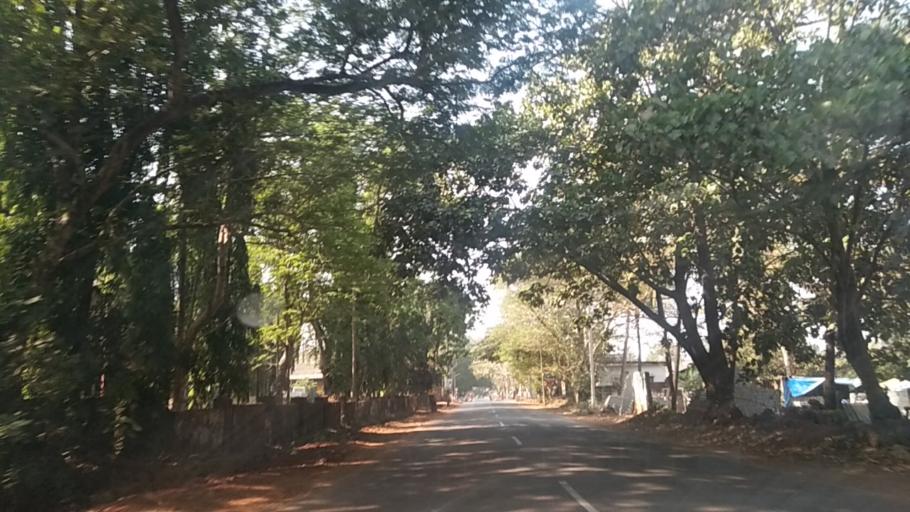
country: IN
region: Goa
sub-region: North Goa
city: Dicholi
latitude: 15.5836
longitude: 73.9615
